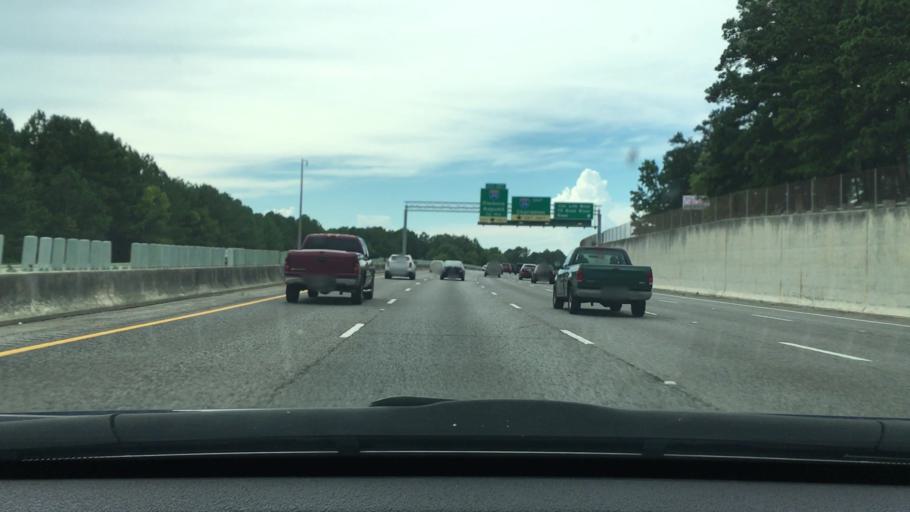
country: US
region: South Carolina
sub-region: Lexington County
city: West Columbia
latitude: 34.0177
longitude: -81.0901
